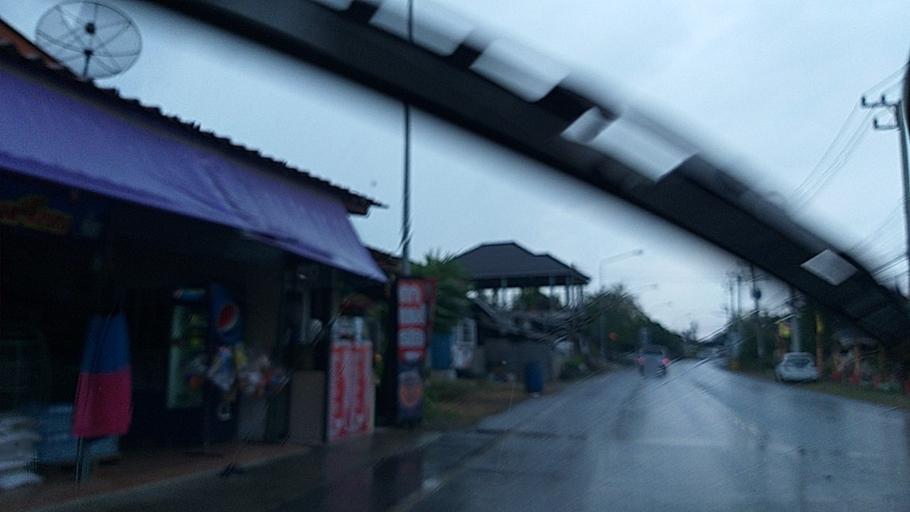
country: TH
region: Phra Nakhon Si Ayutthaya
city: Phra Nakhon Si Ayutthaya
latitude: 14.3396
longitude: 100.5423
